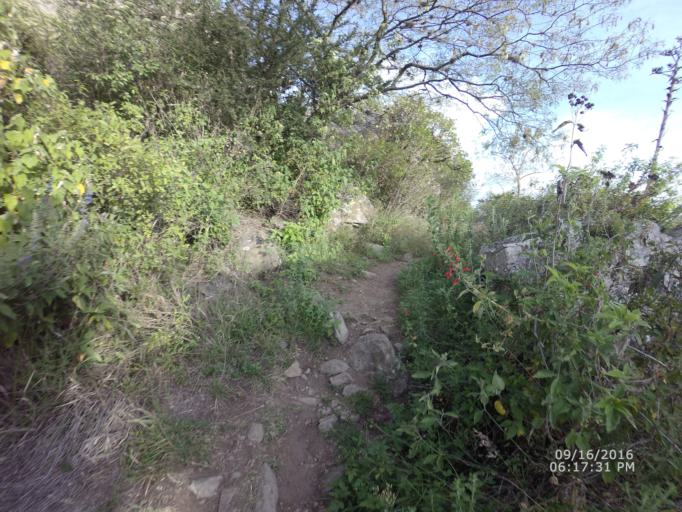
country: MX
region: Queretaro
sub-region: Ezequiel Montes
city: San Jose del Jagueey
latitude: 20.7483
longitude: -99.9500
